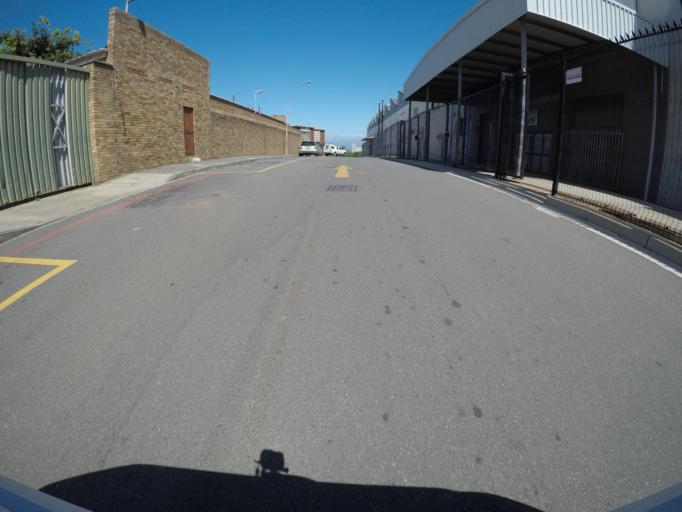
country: ZA
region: Eastern Cape
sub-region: Buffalo City Metropolitan Municipality
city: East London
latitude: -33.0202
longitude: 27.9025
